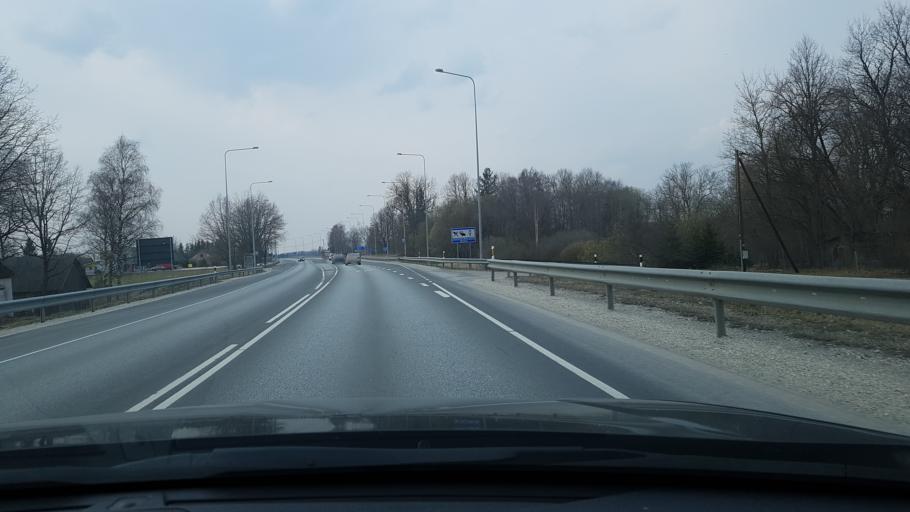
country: EE
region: Tartu
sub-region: Noo vald
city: Noo
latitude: 58.4289
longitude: 26.4876
